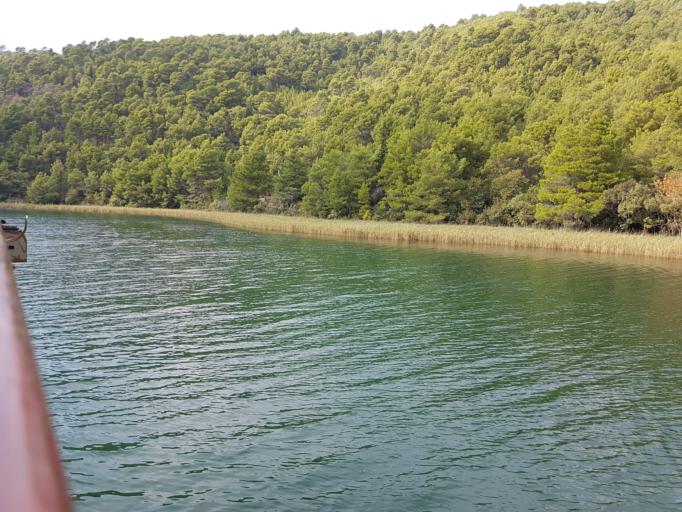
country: HR
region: Sibensko-Kniniska
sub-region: Grad Sibenik
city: Sibenik
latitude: 43.8216
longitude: 15.9444
